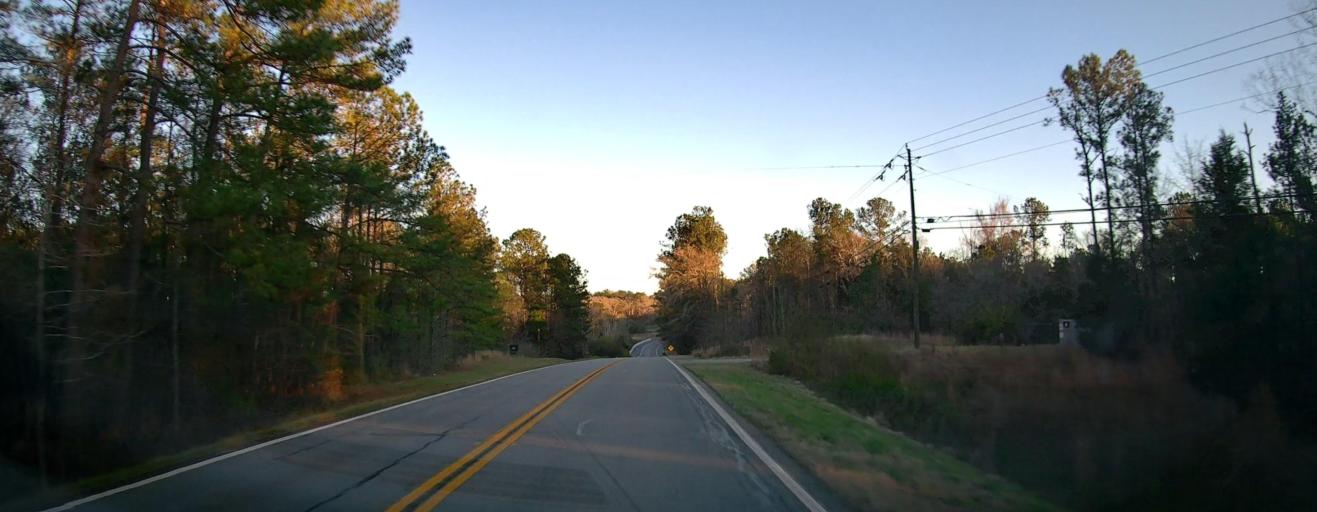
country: US
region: Alabama
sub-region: Lee County
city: Smiths Station
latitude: 32.6204
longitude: -85.0301
